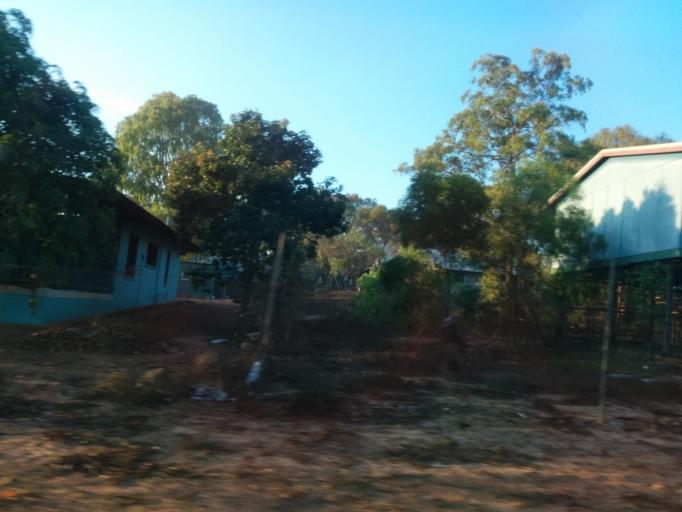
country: AU
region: Northern Territory
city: Alyangula
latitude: -13.8599
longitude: 136.8109
